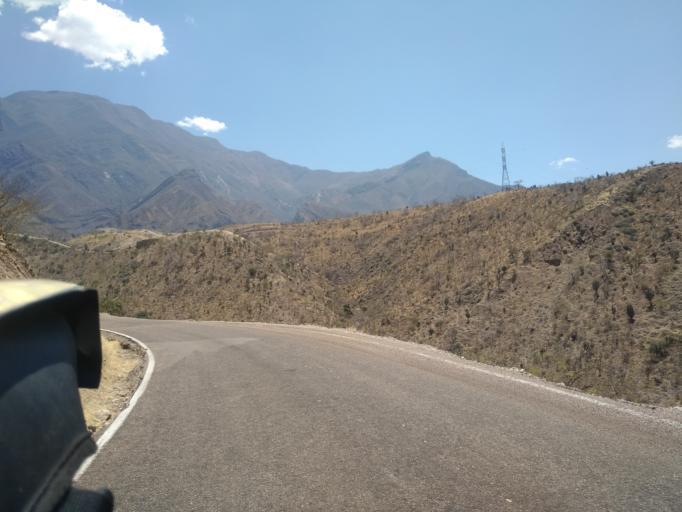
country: PE
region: Amazonas
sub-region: Provincia de Chachapoyas
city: Balsas
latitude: -6.8533
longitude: -78.0337
